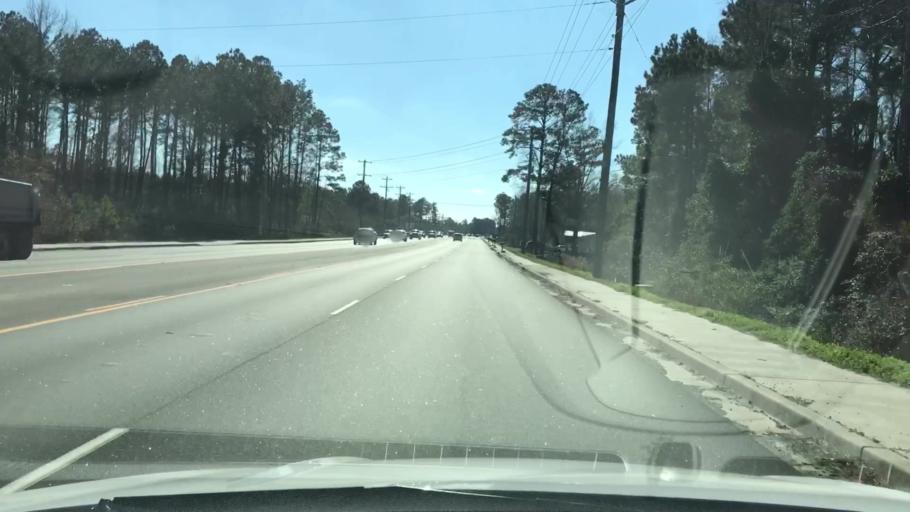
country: US
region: South Carolina
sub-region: Horry County
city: Garden City
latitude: 33.6372
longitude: -79.0330
